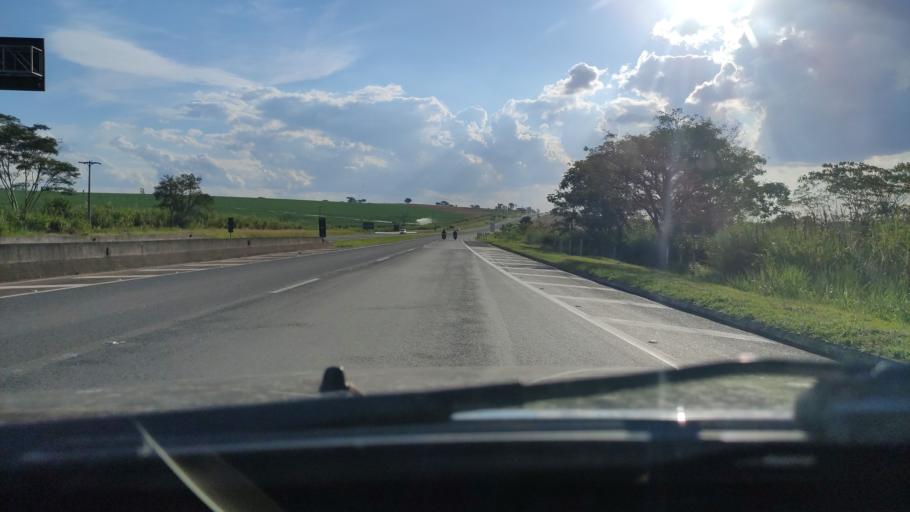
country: BR
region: Sao Paulo
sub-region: Mogi-Mirim
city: Mogi Mirim
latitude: -22.4567
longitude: -46.9037
